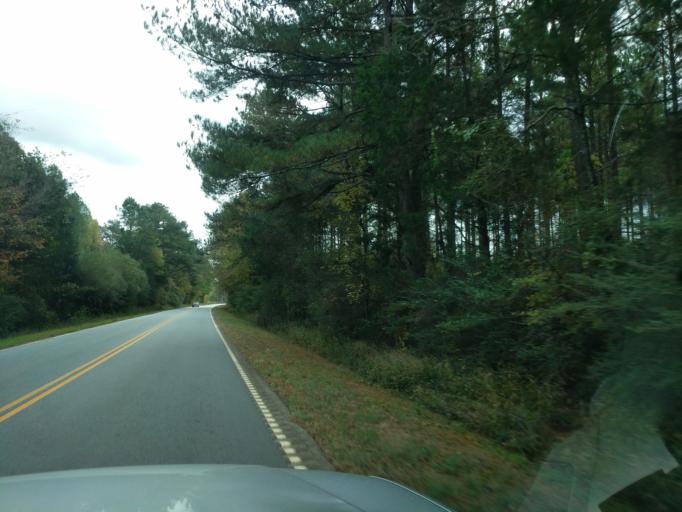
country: US
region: South Carolina
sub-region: Saluda County
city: Saluda
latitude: 34.0426
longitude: -81.8137
